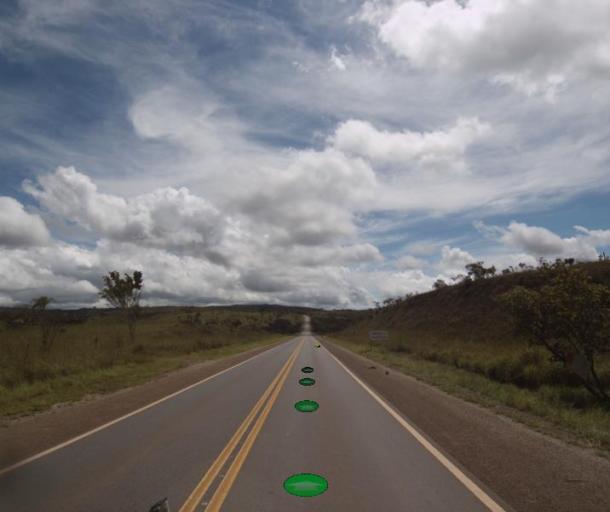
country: BR
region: Federal District
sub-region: Brasilia
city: Brasilia
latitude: -15.7517
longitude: -48.3489
